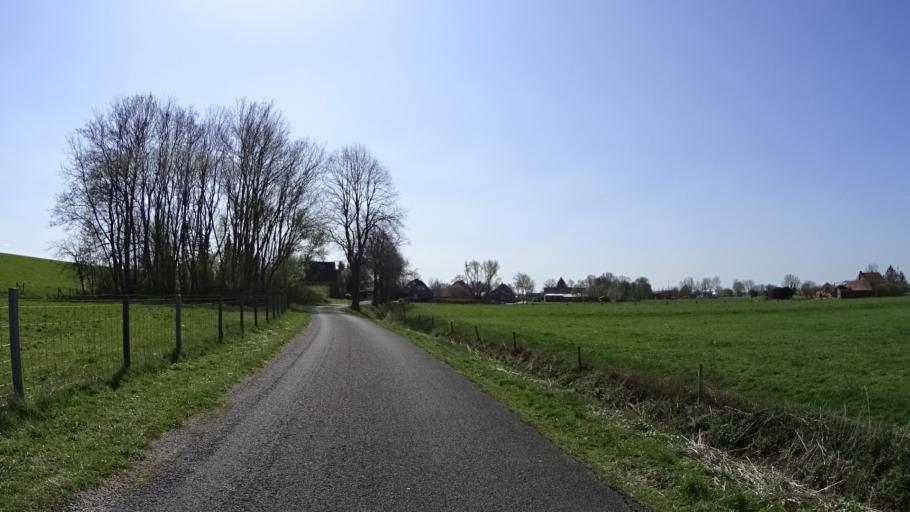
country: DE
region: Lower Saxony
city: Leer
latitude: 53.2048
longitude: 7.4041
